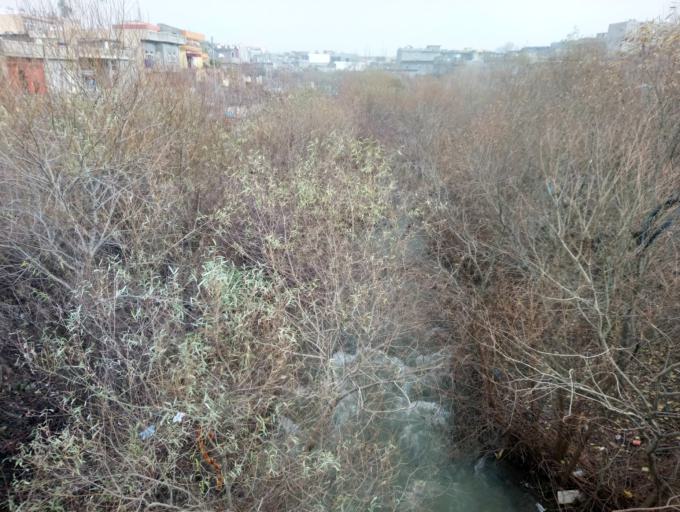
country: IQ
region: As Sulaymaniyah
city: Qeladize
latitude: 36.1788
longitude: 45.1334
